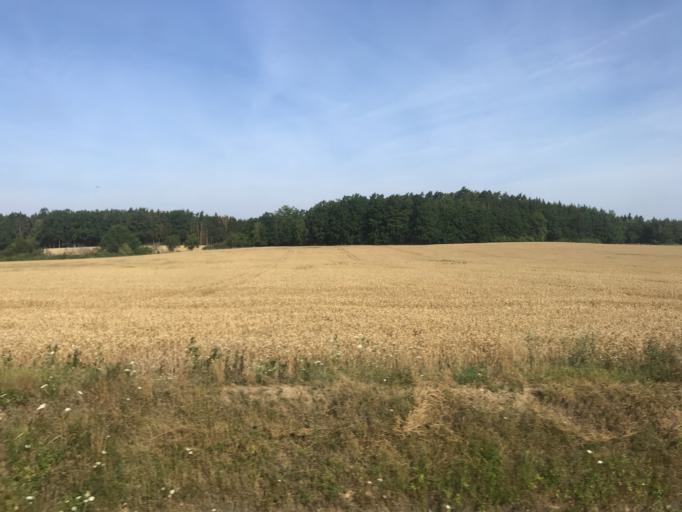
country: CZ
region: Jihocesky
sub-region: Okres Tabor
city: Tabor
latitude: 49.4358
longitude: 14.6875
